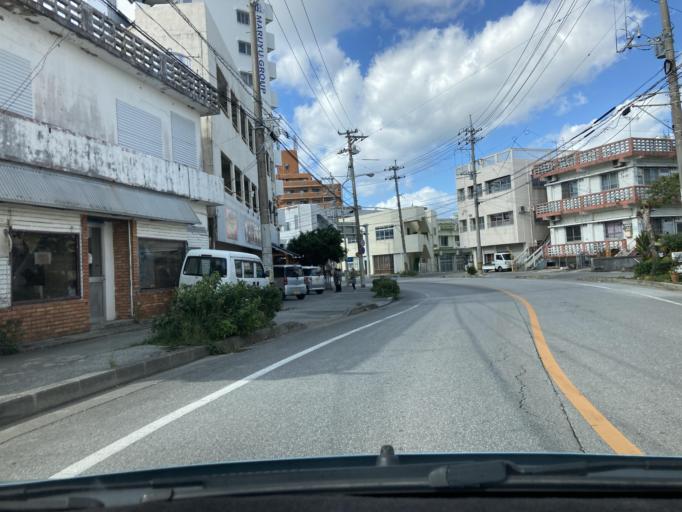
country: JP
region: Okinawa
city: Okinawa
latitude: 26.3227
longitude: 127.7920
